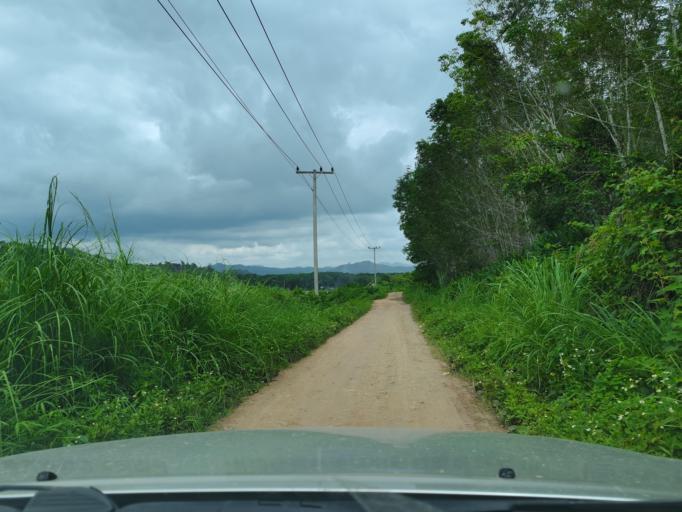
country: LA
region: Loungnamtha
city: Muang Long
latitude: 20.6981
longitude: 101.0373
